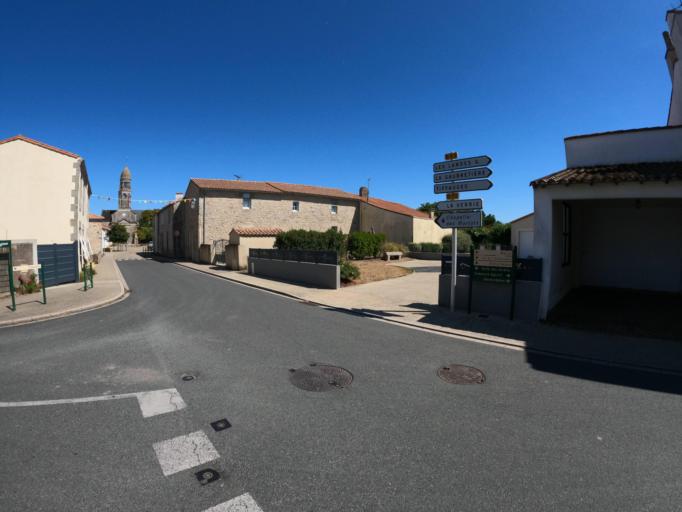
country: FR
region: Pays de la Loire
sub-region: Departement de la Vendee
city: Saint-Aubin-des-Ormeaux
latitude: 46.9738
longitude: -1.0518
